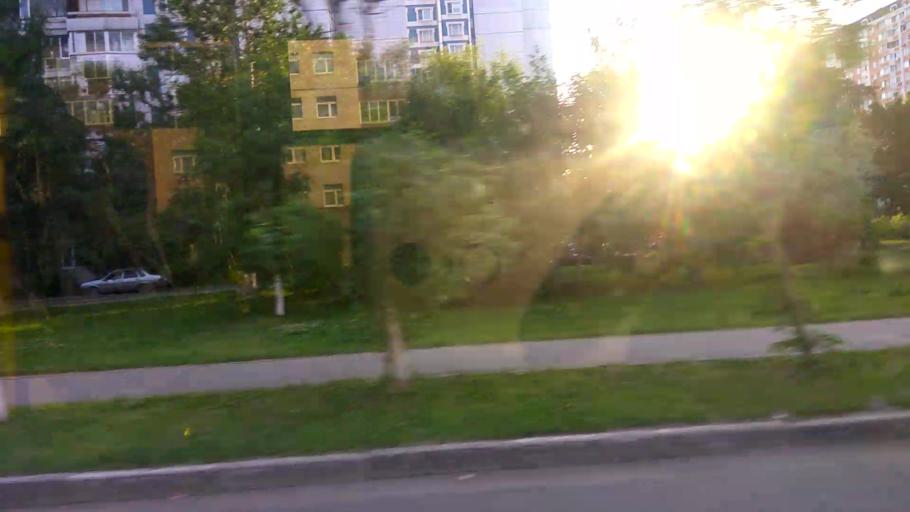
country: RU
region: Moskovskaya
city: Yubileyny
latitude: 55.9122
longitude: 37.8670
